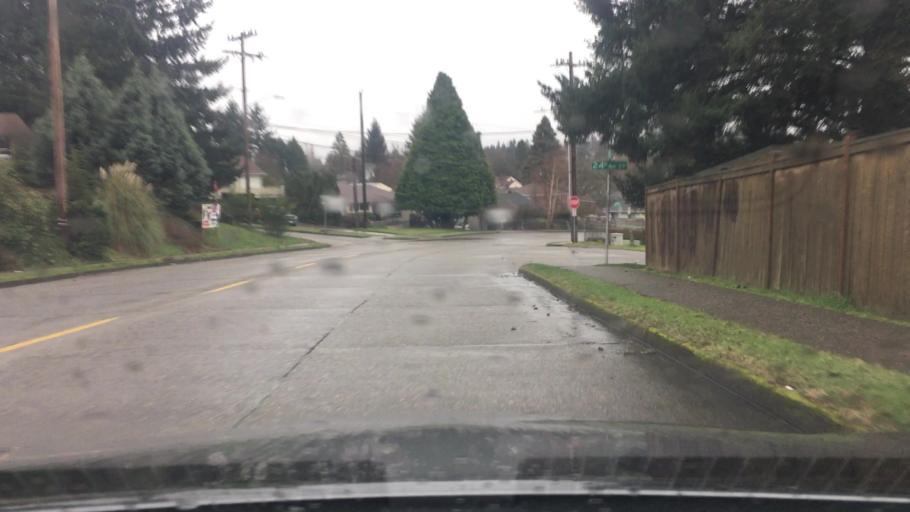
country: US
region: Washington
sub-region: King County
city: White Center
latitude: 47.5215
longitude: -122.3632
